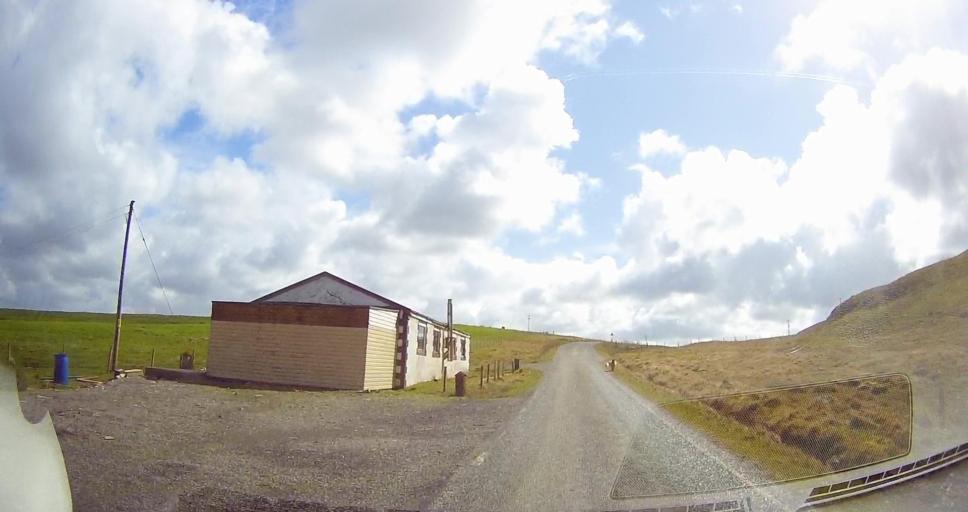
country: GB
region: Scotland
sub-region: Shetland Islands
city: Lerwick
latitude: 60.5450
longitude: -1.3413
